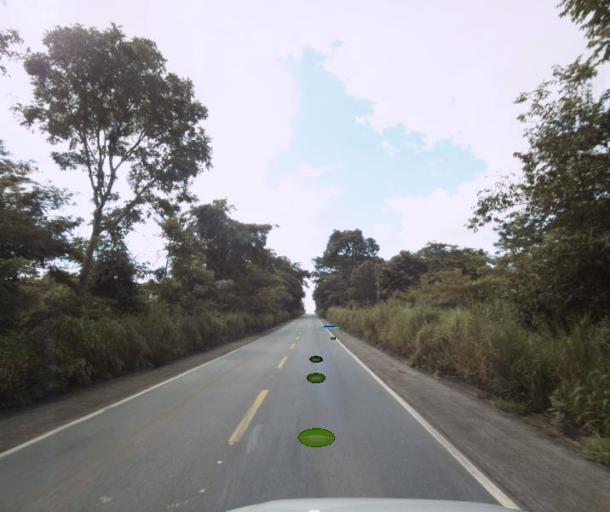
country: BR
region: Goias
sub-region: Porangatu
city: Porangatu
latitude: -13.1311
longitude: -49.1938
